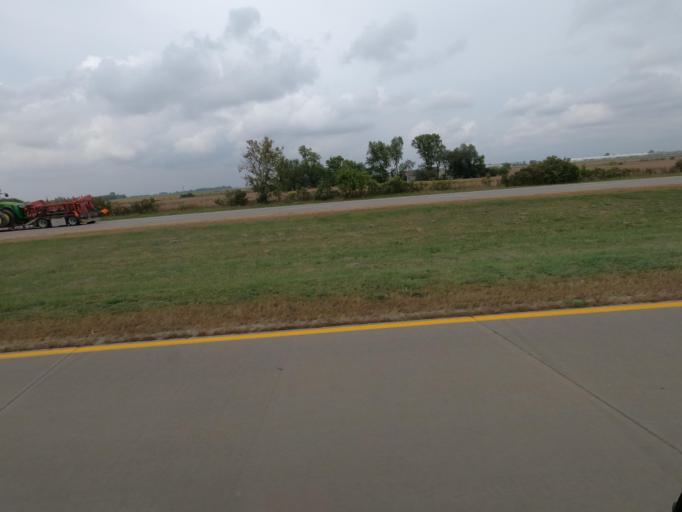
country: US
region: Iowa
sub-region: Wapello County
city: Ottumwa
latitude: 41.0951
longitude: -92.4493
